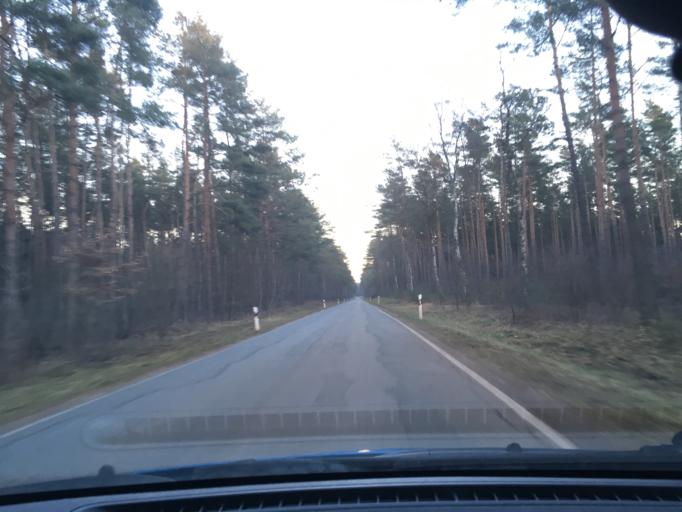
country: DE
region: Schleswig-Holstein
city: Brothen
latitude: 53.4843
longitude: 10.6872
